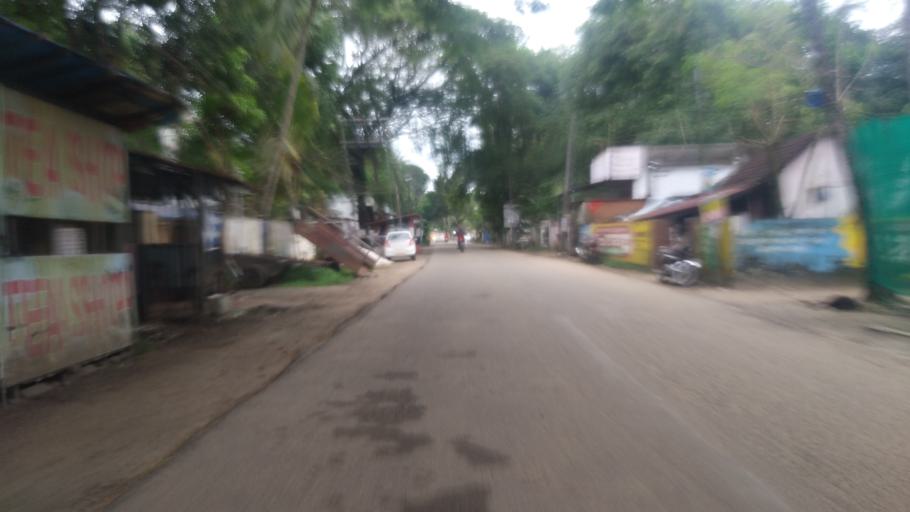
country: IN
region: Kerala
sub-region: Alappuzha
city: Arukutti
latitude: 9.8693
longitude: 76.2908
